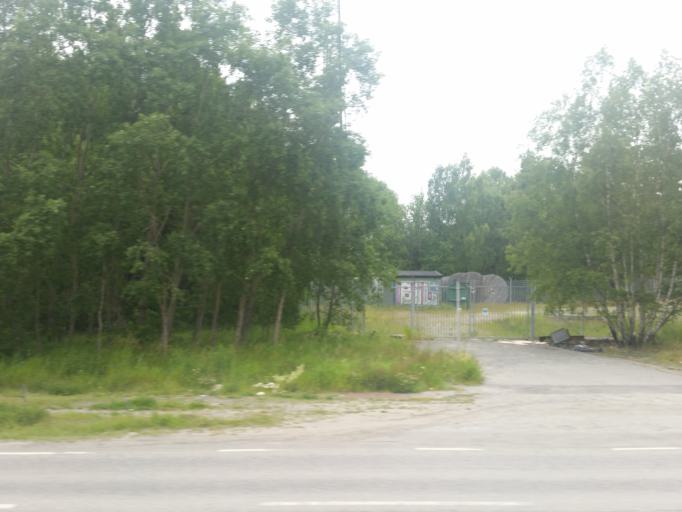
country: SE
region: Stockholm
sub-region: Stockholms Kommun
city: Kista
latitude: 59.4147
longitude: 17.9032
